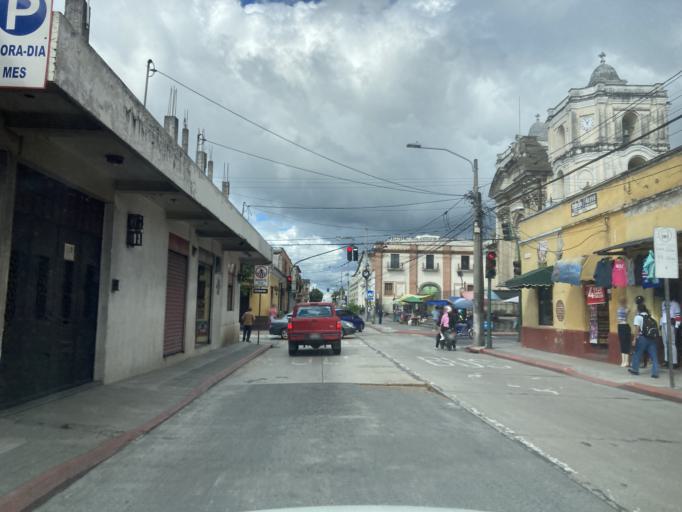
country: GT
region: Guatemala
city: Guatemala City
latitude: 14.6422
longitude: -90.5081
